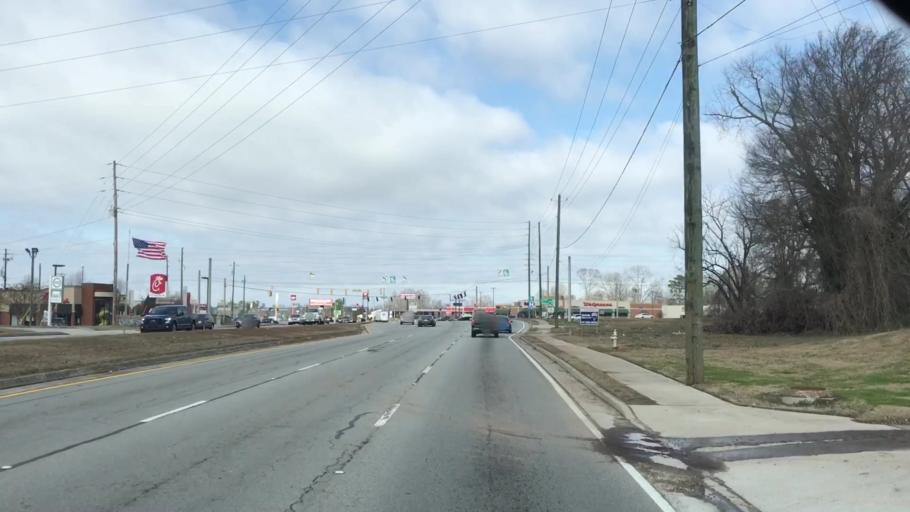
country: US
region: Georgia
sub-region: Hall County
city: Oakwood
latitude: 34.2190
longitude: -83.8617
